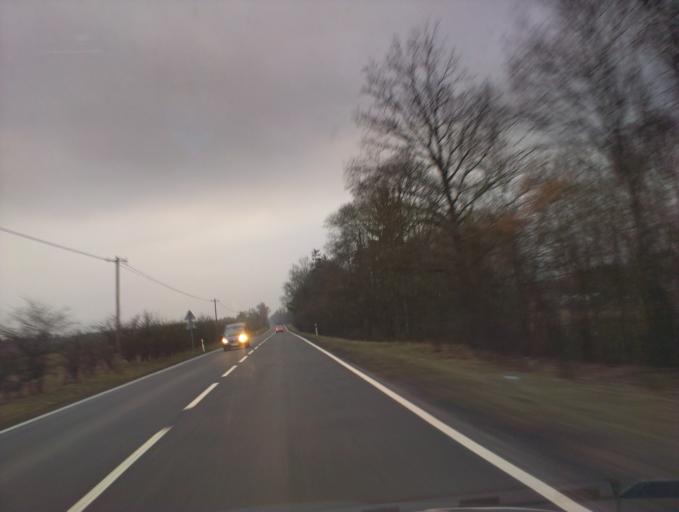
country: PL
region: Greater Poland Voivodeship
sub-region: Powiat zlotowski
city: Jastrowie
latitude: 53.3680
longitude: 16.7867
